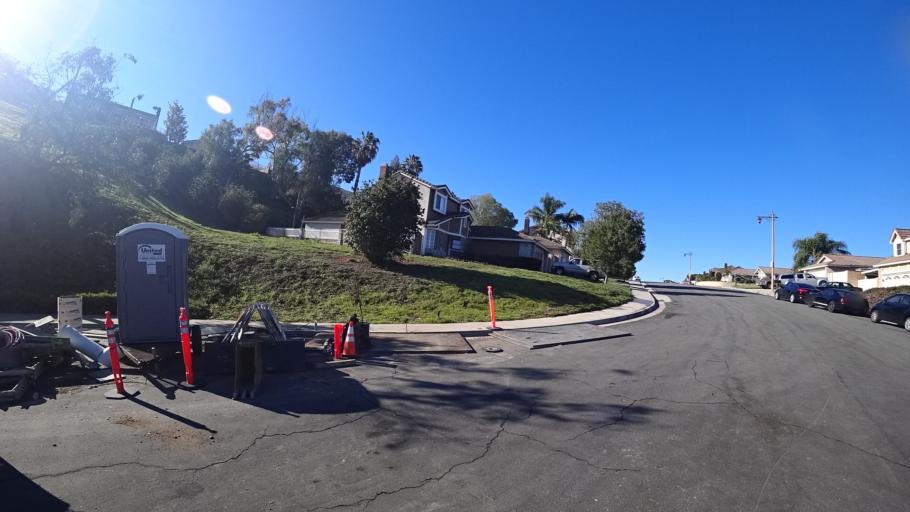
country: US
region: California
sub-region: Orange County
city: Yorba Linda
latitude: 33.8679
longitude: -117.7363
